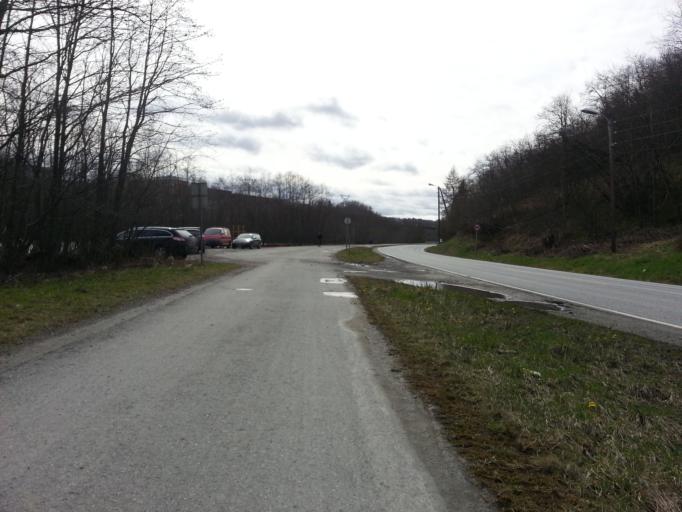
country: NO
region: Sor-Trondelag
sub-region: Trondheim
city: Trondheim
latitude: 63.4005
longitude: 10.3885
